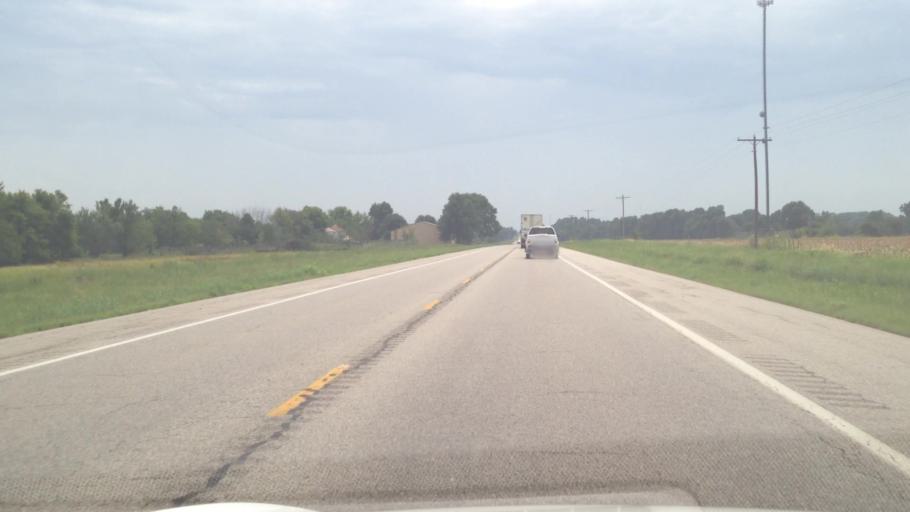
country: US
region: Missouri
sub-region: Jasper County
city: Carl Junction
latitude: 37.2118
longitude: -94.7046
